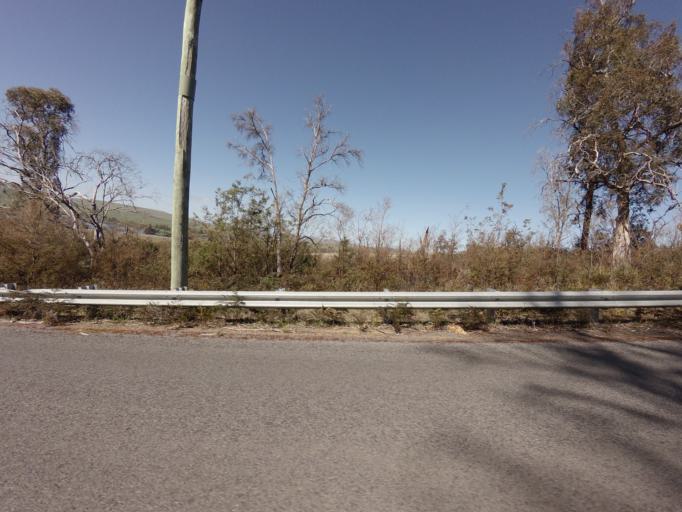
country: AU
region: Tasmania
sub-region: Derwent Valley
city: New Norfolk
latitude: -42.5398
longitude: 146.7208
